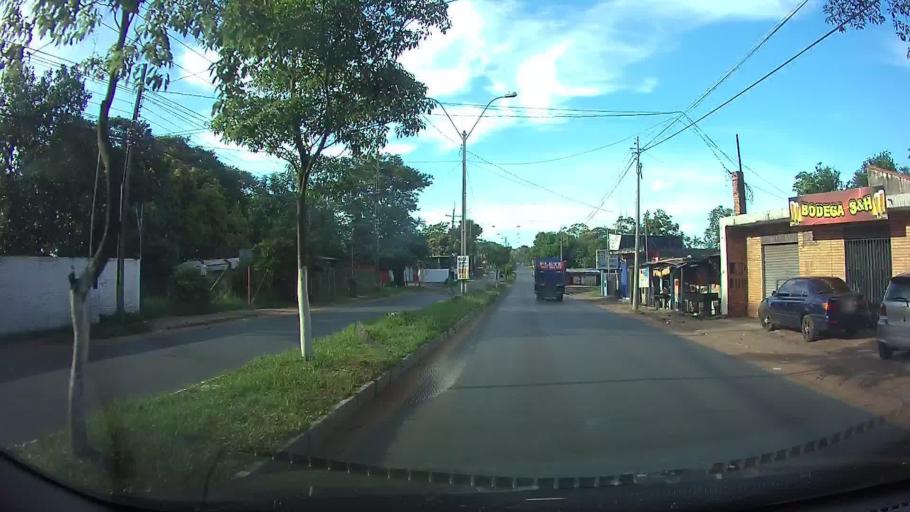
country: PY
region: Central
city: Villa Elisa
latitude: -25.3916
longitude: -57.5824
